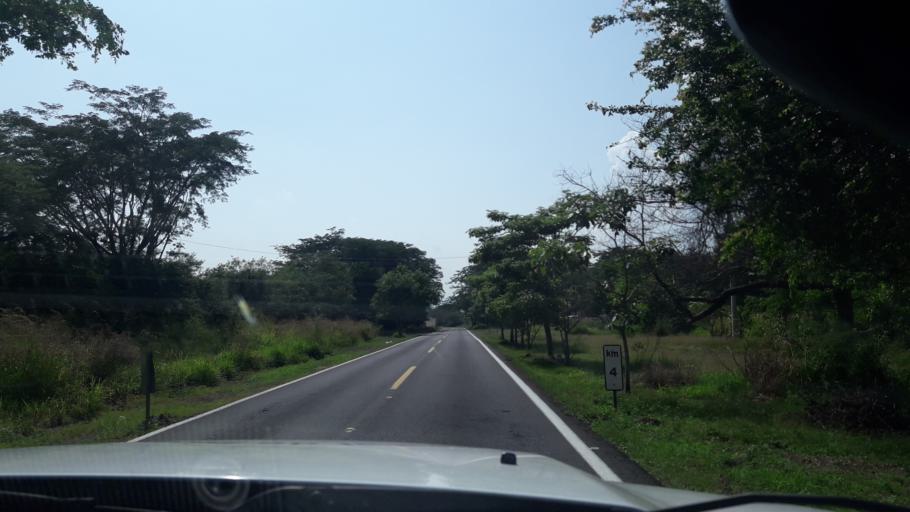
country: MX
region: Colima
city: Comala
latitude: 19.3492
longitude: -103.7364
